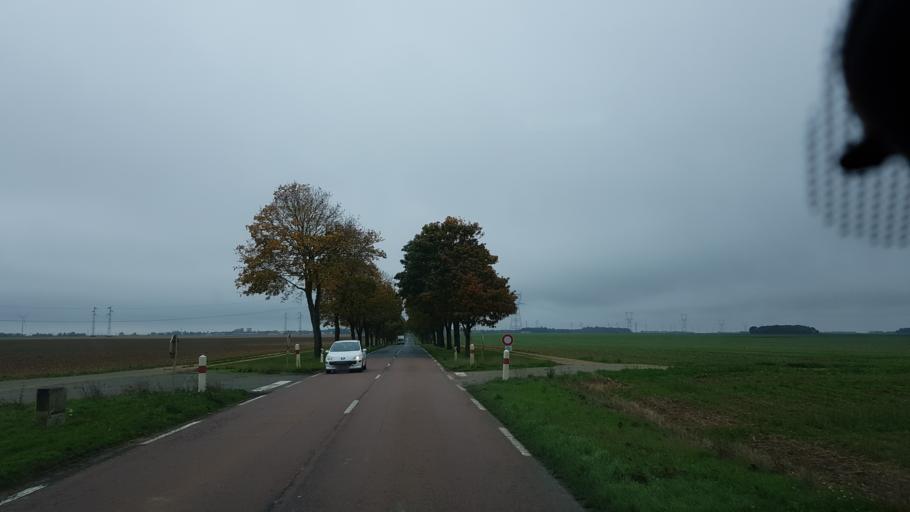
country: FR
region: Ile-de-France
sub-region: Departement de l'Essonne
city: Pussay
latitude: 48.3418
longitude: 1.9891
